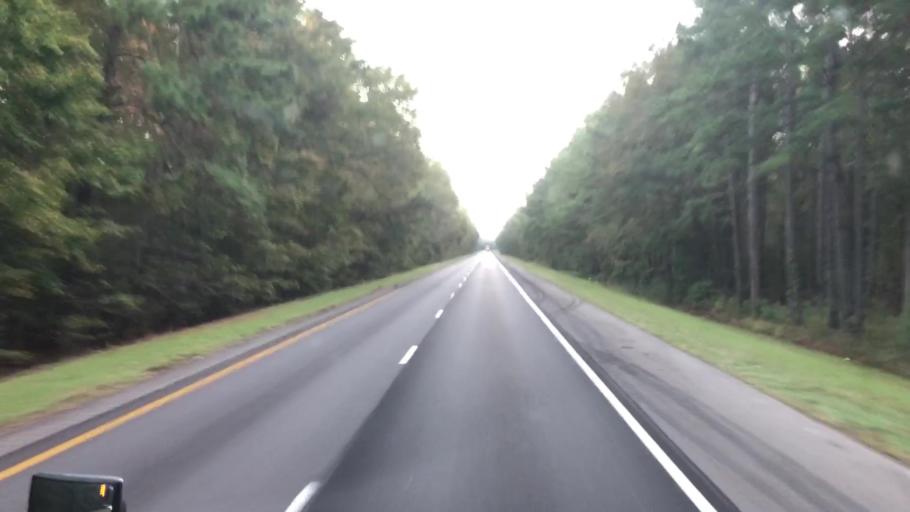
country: US
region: South Carolina
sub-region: Orangeburg County
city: Holly Hill
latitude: 33.5421
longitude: -80.4138
